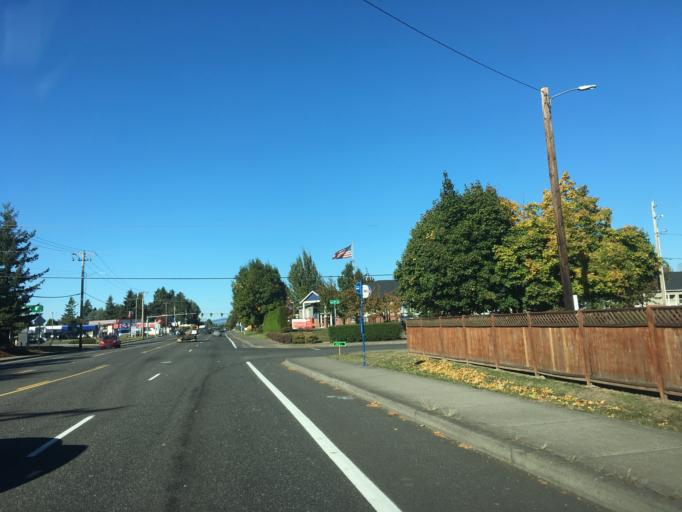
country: US
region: Oregon
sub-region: Multnomah County
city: Gresham
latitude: 45.5029
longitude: -122.3999
